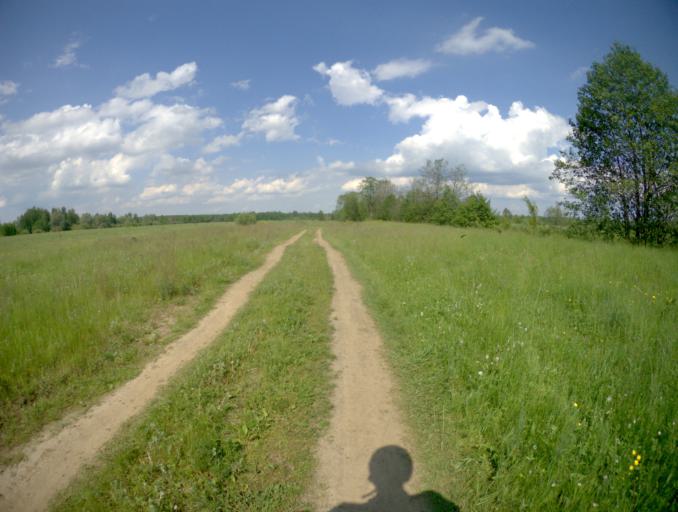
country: RU
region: Vladimir
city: Raduzhnyy
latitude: 56.0411
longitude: 40.3109
